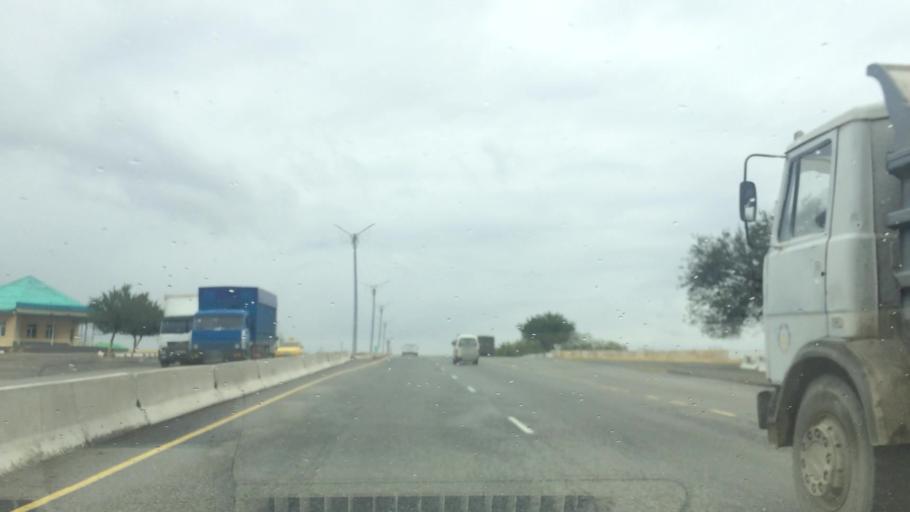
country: UZ
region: Samarqand
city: Bulung'ur
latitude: 39.8546
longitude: 67.4655
